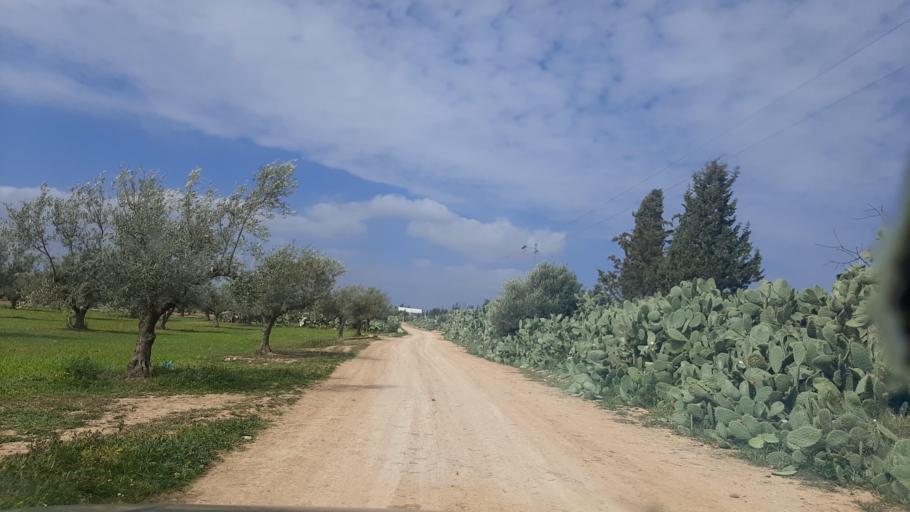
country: TN
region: Tunis
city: La Mohammedia
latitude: 36.6847
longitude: 10.0115
